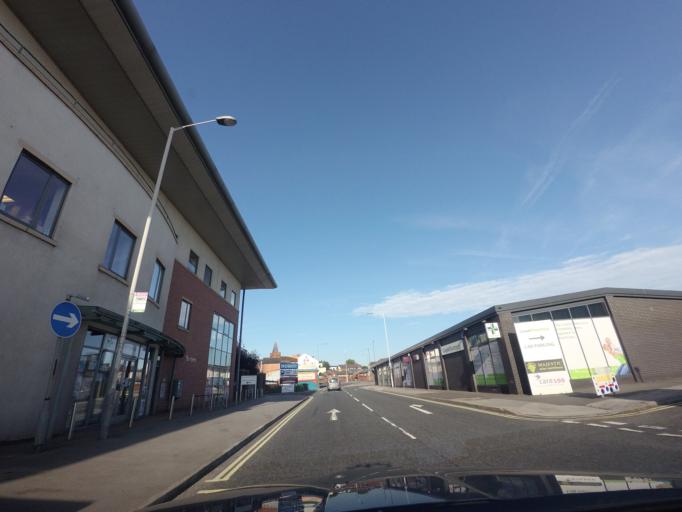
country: GB
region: England
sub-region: Derbyshire
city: Chesterfield
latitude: 53.2349
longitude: -1.4399
